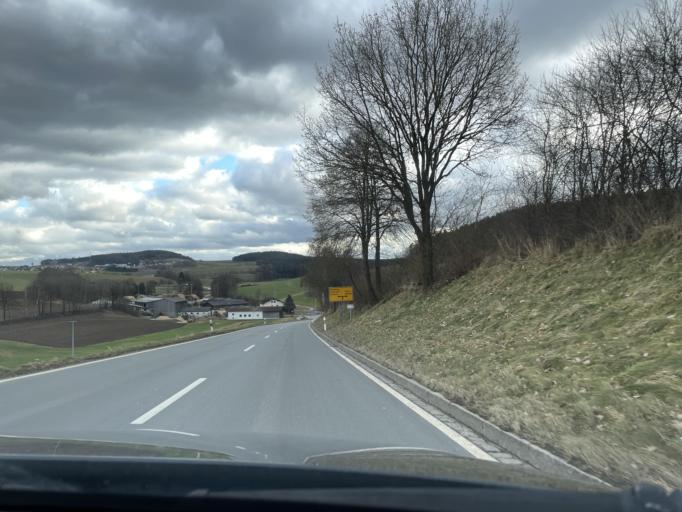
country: DE
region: Bavaria
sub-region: Upper Palatinate
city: Runding
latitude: 49.2050
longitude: 12.7742
